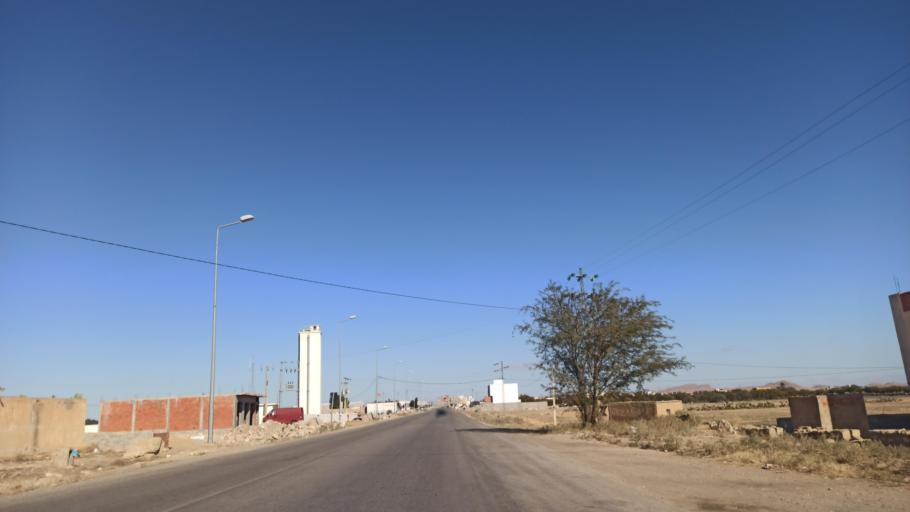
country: TN
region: Sidi Bu Zayd
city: Jilma
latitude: 35.2599
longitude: 9.4047
